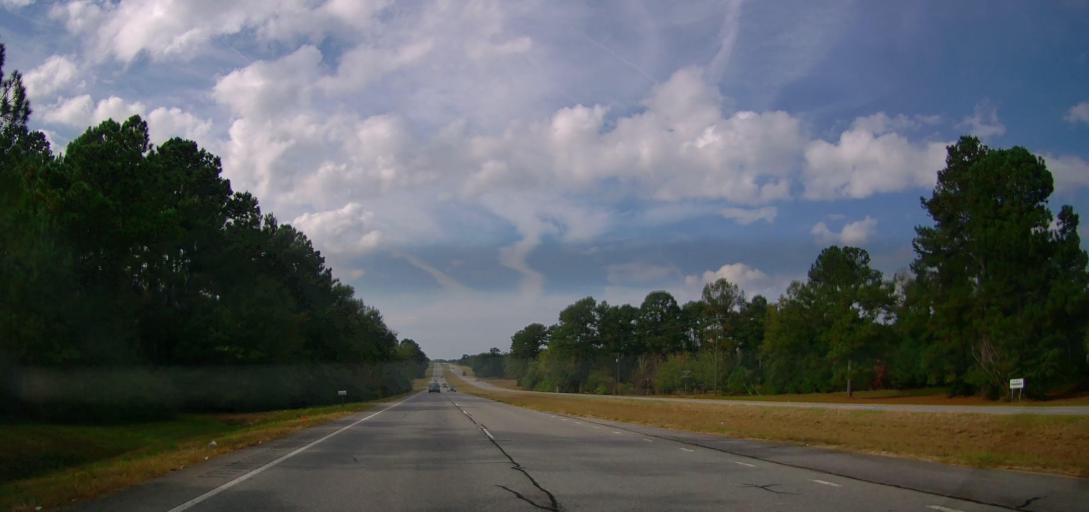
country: US
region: Georgia
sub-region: Thomas County
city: Meigs
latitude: 31.1029
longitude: -84.1071
